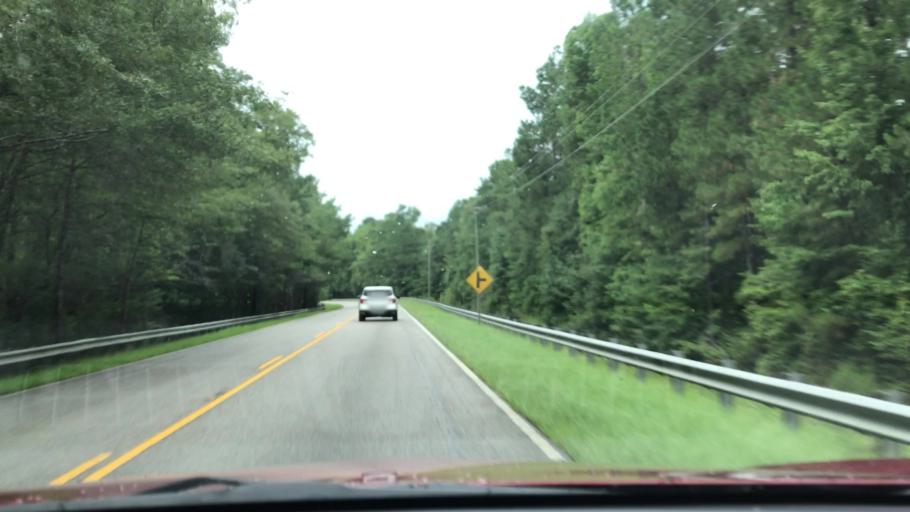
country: US
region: South Carolina
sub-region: Georgetown County
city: Murrells Inlet
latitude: 33.6177
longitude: -79.1948
